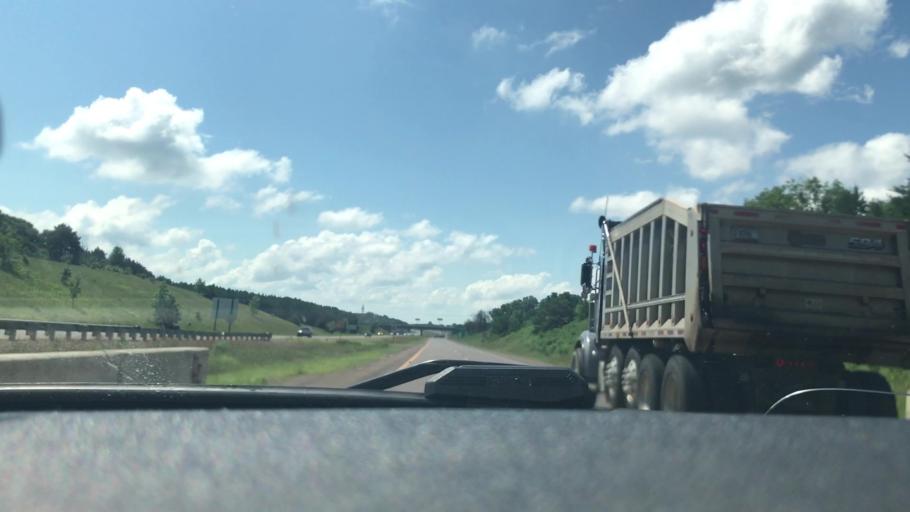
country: US
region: Wisconsin
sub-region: Chippewa County
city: Chippewa Falls
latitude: 44.9210
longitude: -91.4283
